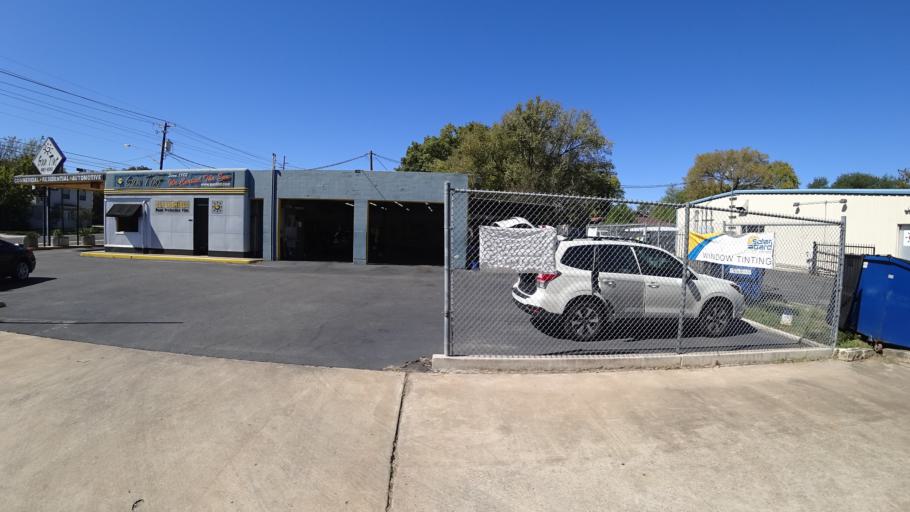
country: US
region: Texas
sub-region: Travis County
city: Austin
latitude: 30.3327
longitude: -97.7346
